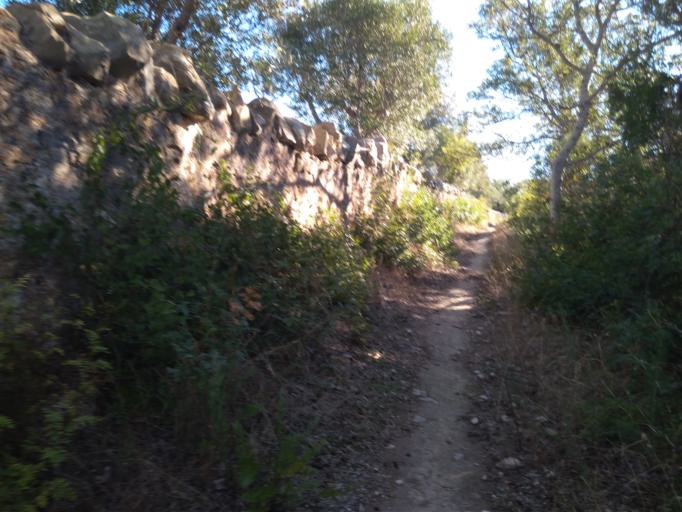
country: PT
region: Faro
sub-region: Faro
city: Santa Barbara de Nexe
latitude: 37.1013
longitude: -7.9577
